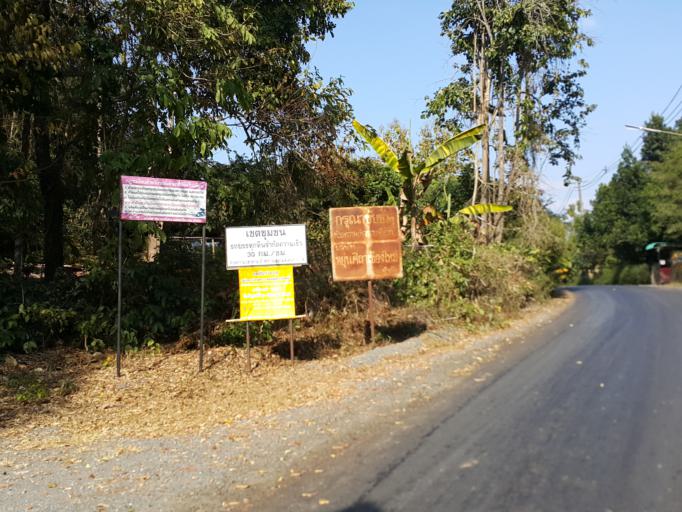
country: TH
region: Chiang Mai
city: Mae On
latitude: 18.8299
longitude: 99.2062
